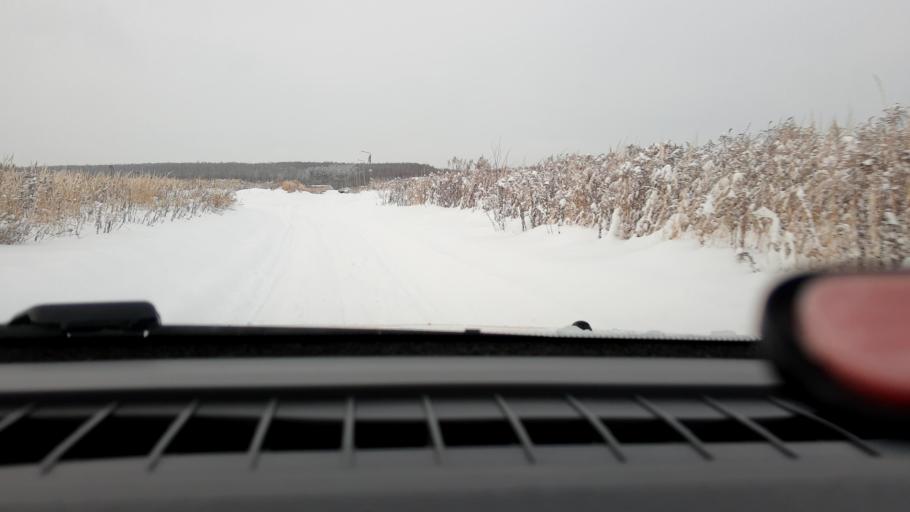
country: RU
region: Nizjnij Novgorod
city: Afonino
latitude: 56.1333
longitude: 43.9909
